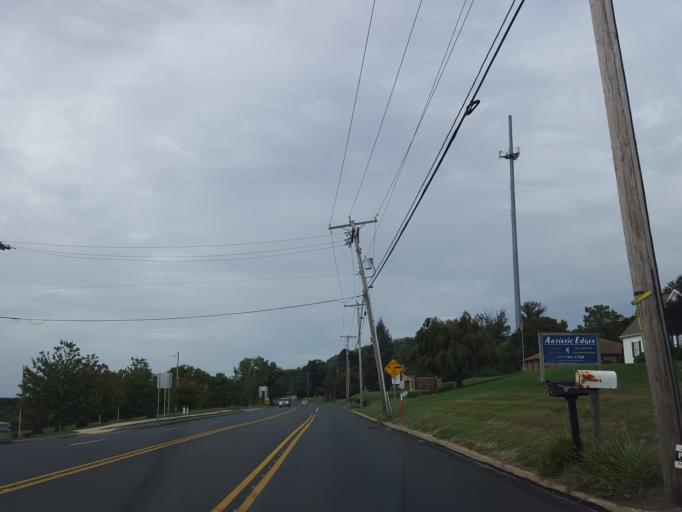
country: US
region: Pennsylvania
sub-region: York County
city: Spry
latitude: 39.9112
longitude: -76.6831
